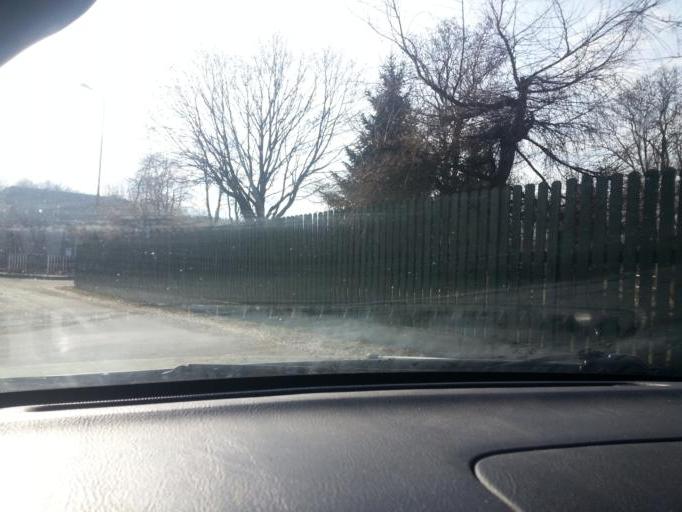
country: PL
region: Lower Silesian Voivodeship
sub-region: Jelenia Gora
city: Cieplice Slaskie Zdroj
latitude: 50.8792
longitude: 15.7072
